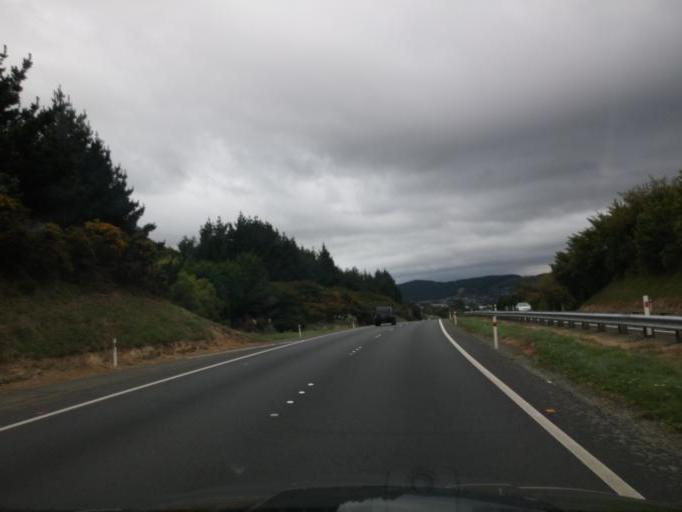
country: NZ
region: Wellington
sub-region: Porirua City
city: Porirua
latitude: -41.1555
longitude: 174.8392
